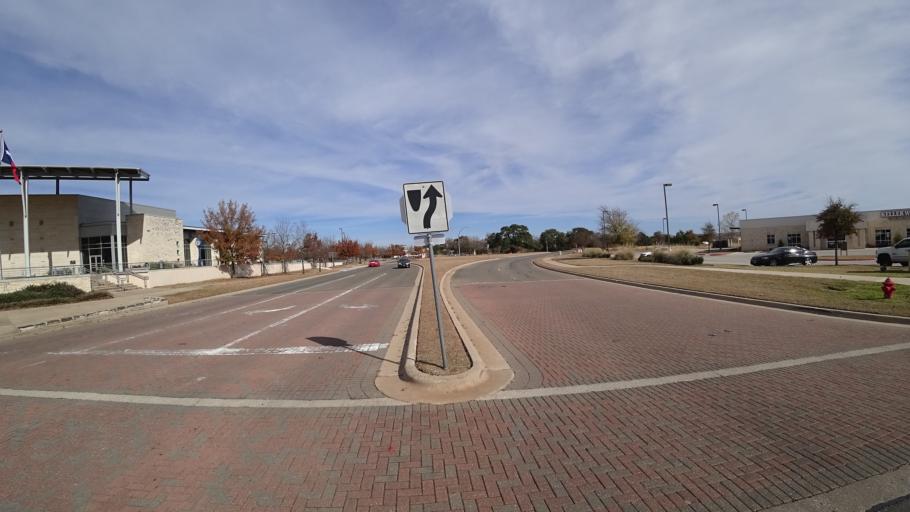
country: US
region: Texas
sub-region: Williamson County
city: Cedar Park
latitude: 30.5197
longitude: -97.8240
